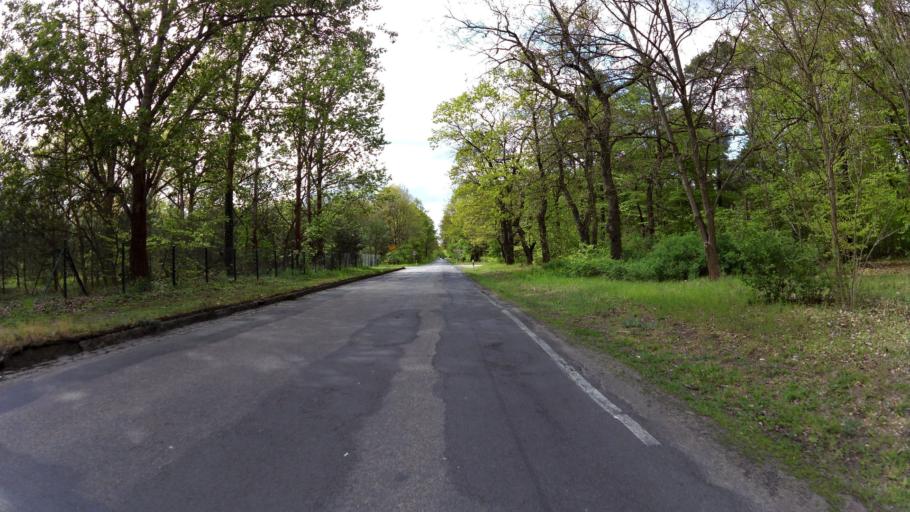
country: DE
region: Brandenburg
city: Furstenwalde
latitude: 52.3590
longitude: 14.0406
